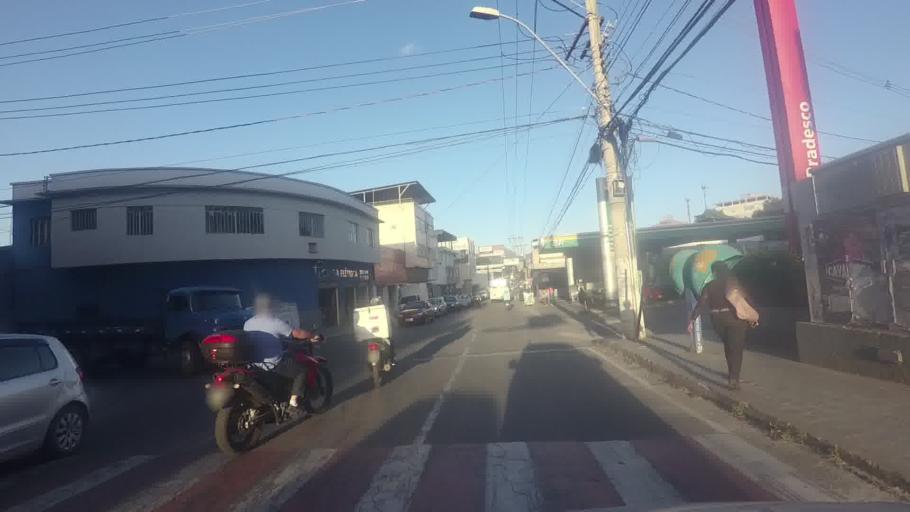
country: BR
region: Espirito Santo
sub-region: Cachoeiro De Itapemirim
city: Cachoeiro de Itapemirim
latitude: -20.8446
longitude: -41.1293
